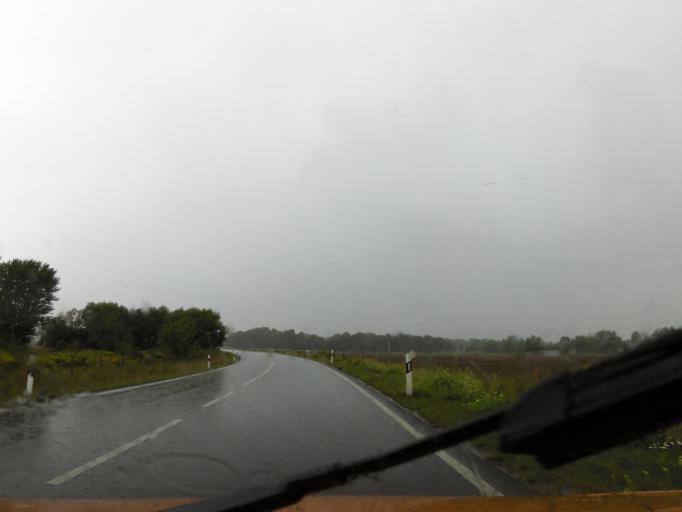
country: DE
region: Brandenburg
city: Werder
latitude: 52.4396
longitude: 12.9883
